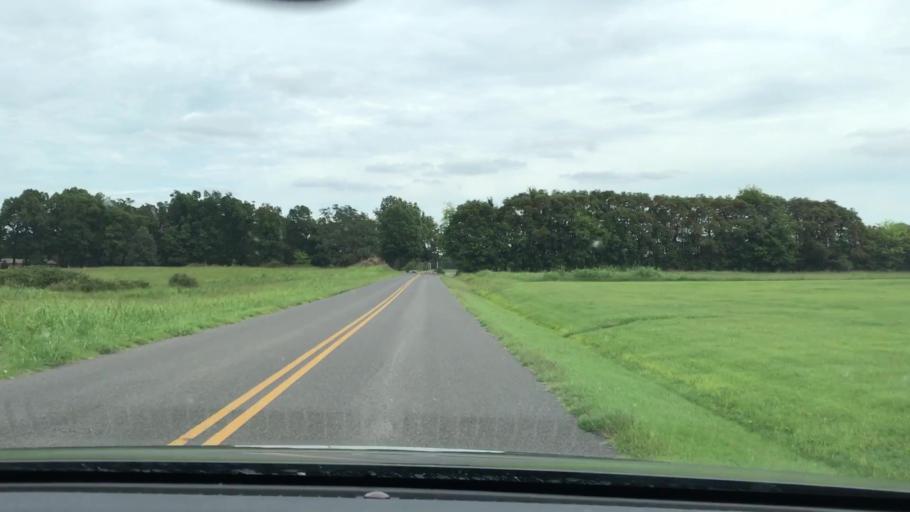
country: US
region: Kentucky
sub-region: Marshall County
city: Benton
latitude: 36.8313
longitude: -88.3549
